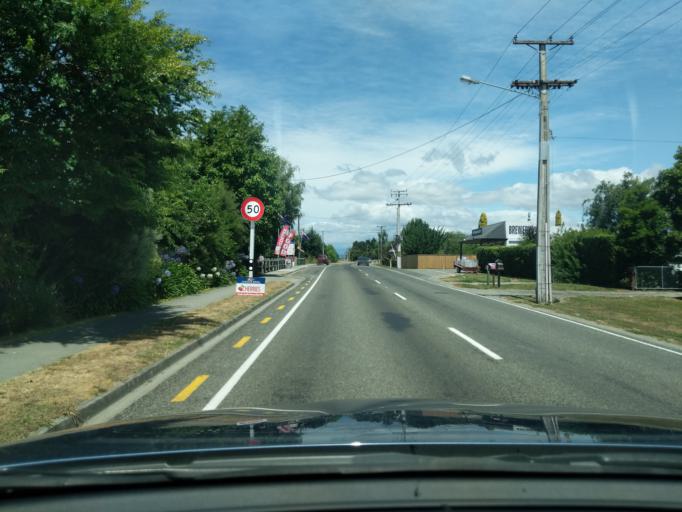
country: NZ
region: Tasman
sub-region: Tasman District
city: Motueka
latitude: -41.0794
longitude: 172.9973
